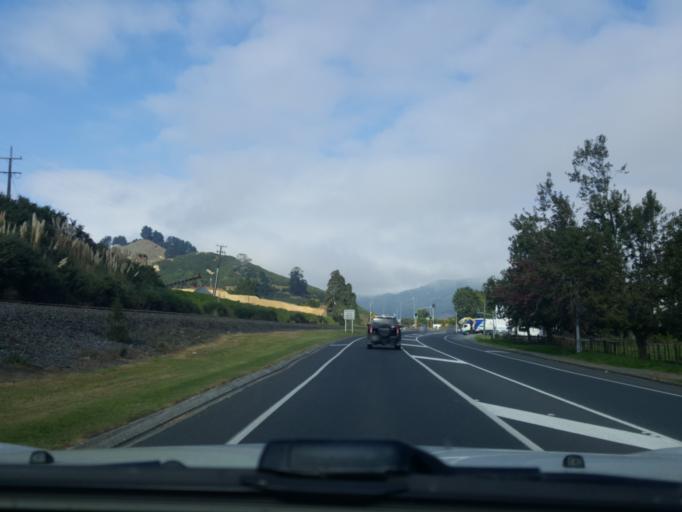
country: NZ
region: Waikato
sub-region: Waikato District
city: Ngaruawahia
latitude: -37.5760
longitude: 175.1598
